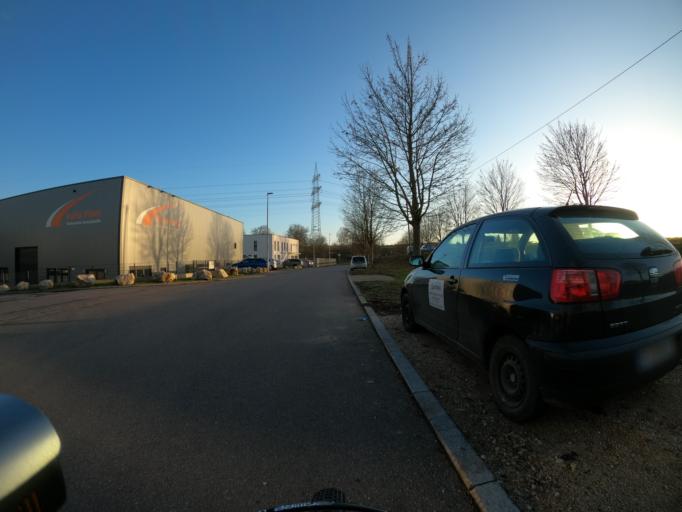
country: DE
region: Baden-Wuerttemberg
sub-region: Regierungsbezirk Stuttgart
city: Wernau
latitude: 48.6789
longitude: 9.4285
